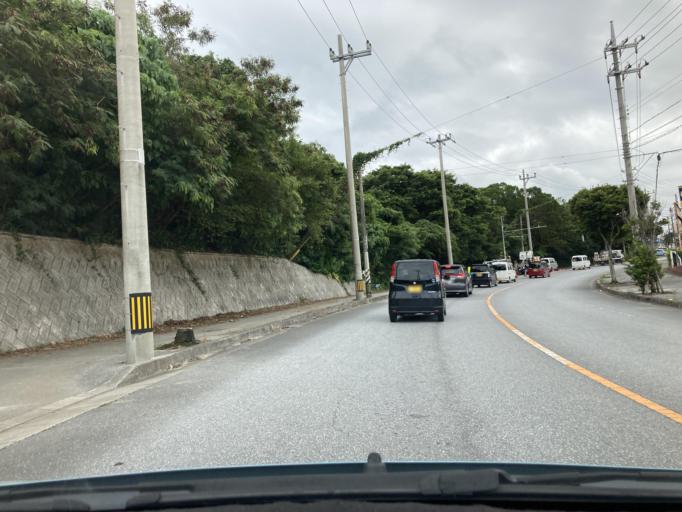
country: JP
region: Okinawa
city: Ginowan
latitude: 26.2448
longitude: 127.7644
